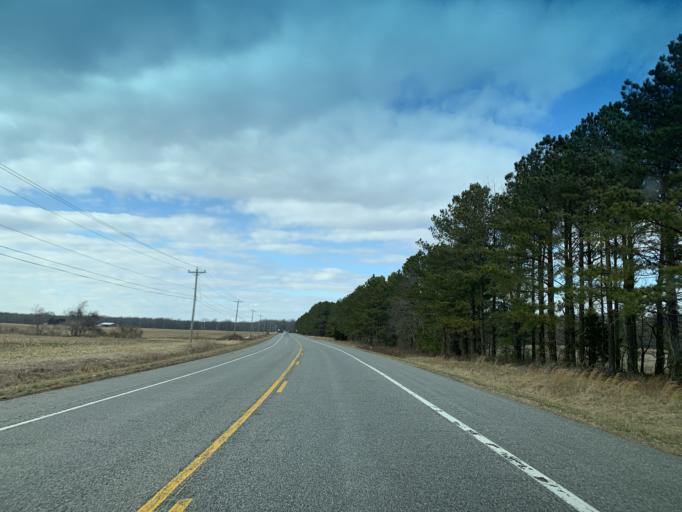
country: US
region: Maryland
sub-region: Queen Anne's County
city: Centreville
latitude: 38.9784
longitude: -76.0699
